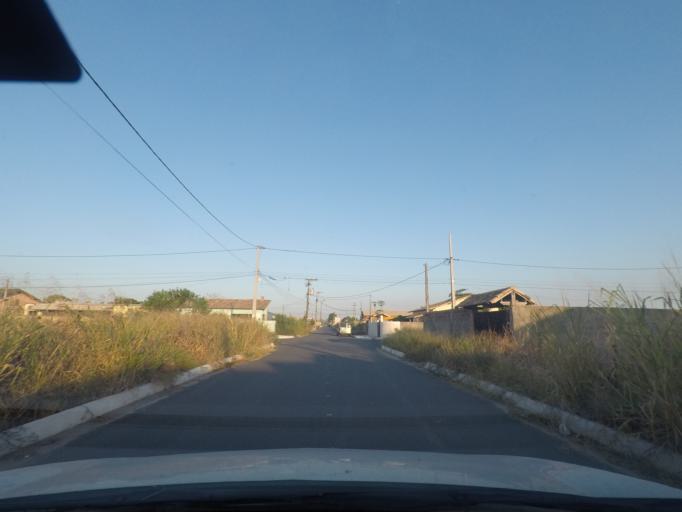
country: BR
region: Rio de Janeiro
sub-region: Marica
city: Marica
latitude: -22.9594
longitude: -42.9383
